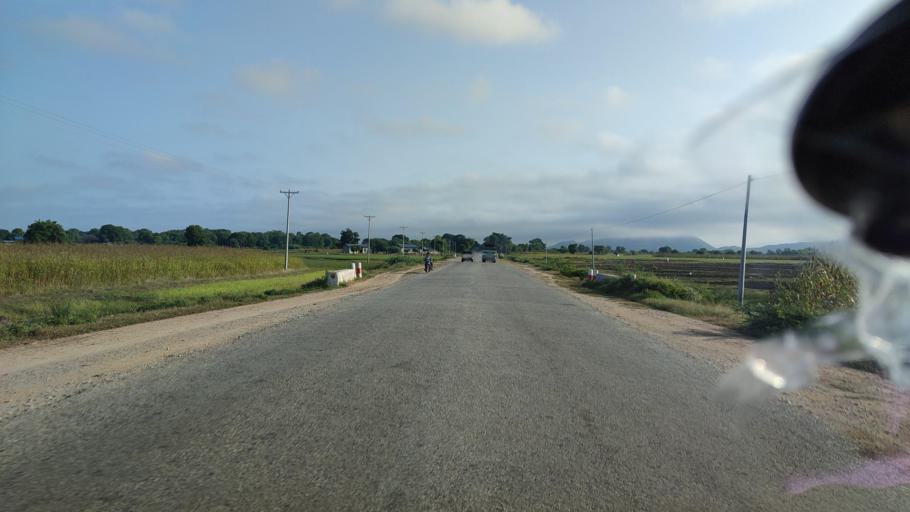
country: MM
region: Mandalay
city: Yamethin
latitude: 20.6888
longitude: 96.1592
